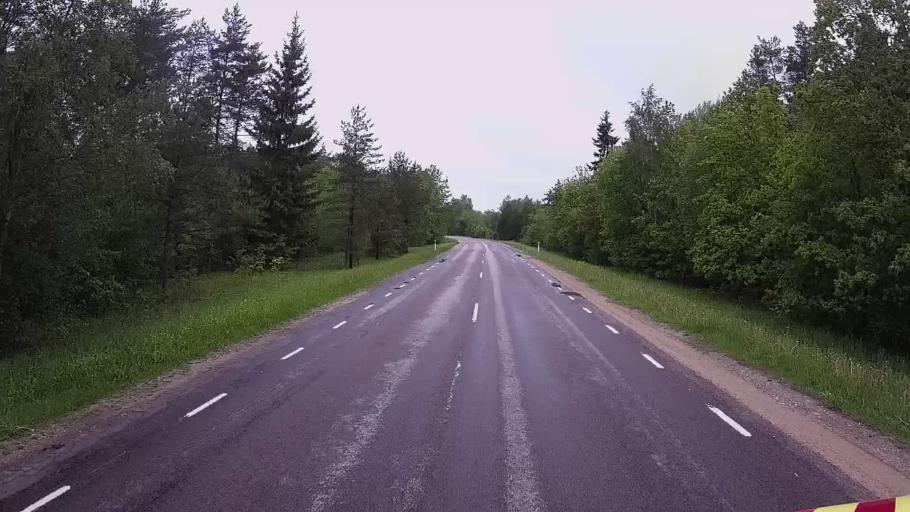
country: EE
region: Harju
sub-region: Nissi vald
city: Turba
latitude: 58.9122
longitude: 24.2027
